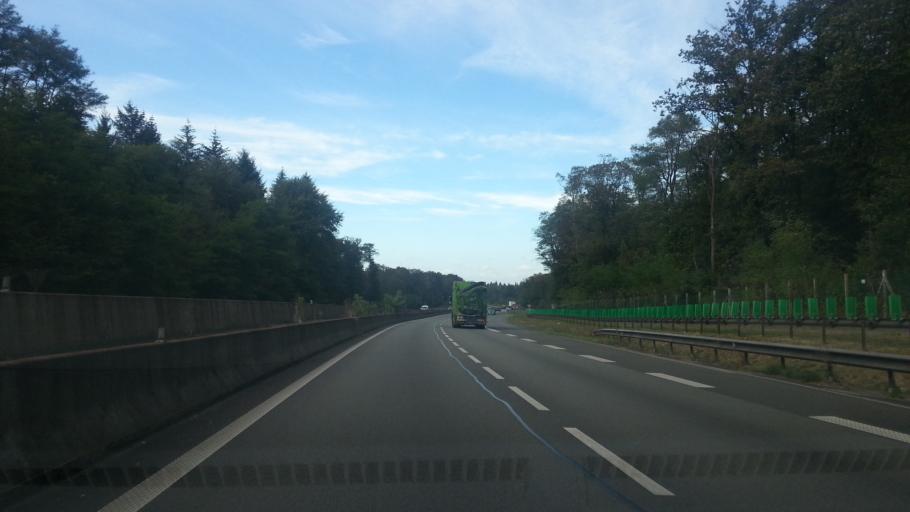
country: FR
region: Picardie
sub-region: Departement de l'Oise
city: Avilly-Saint-Leonard
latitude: 49.2281
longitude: 2.5410
